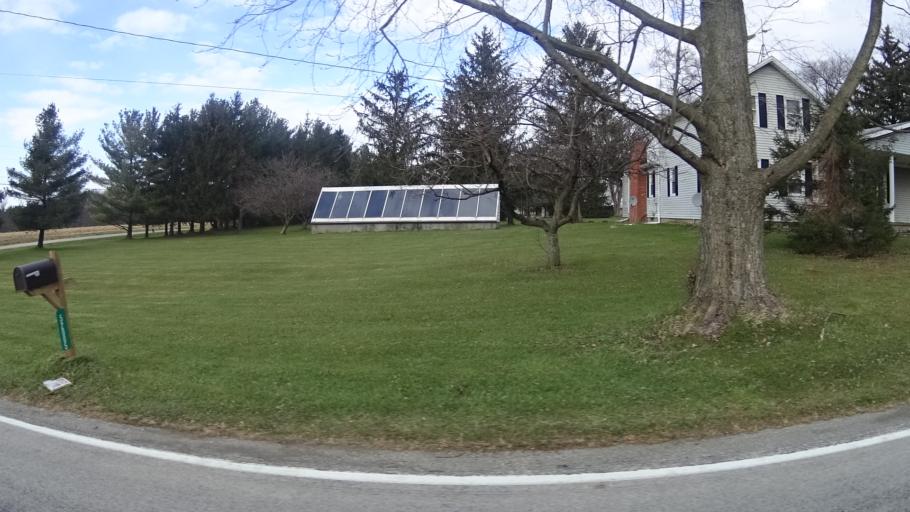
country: US
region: Ohio
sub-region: Lorain County
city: Camden
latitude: 41.2761
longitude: -82.3287
